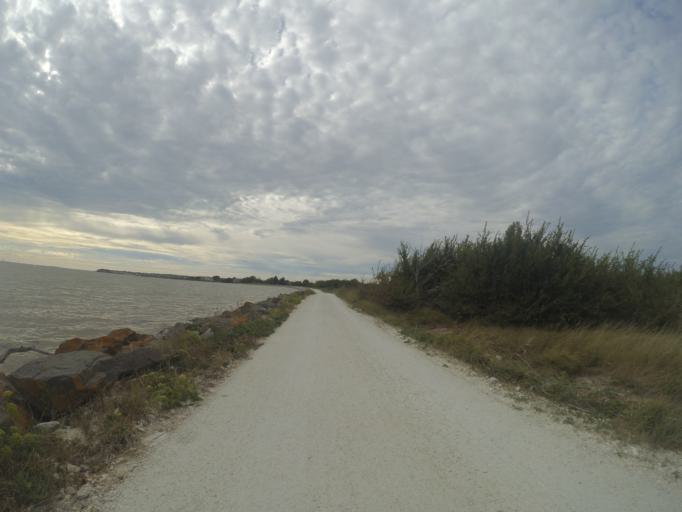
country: FR
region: Poitou-Charentes
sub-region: Departement de la Charente-Maritime
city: Meschers-sur-Gironde
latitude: 45.5492
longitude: -0.9149
